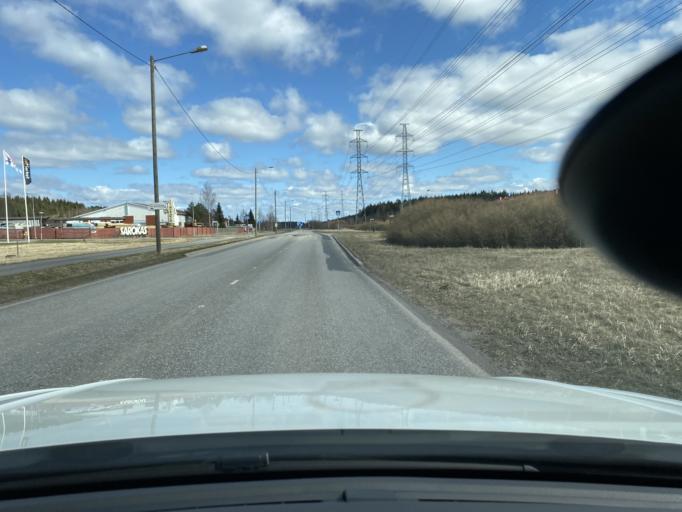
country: FI
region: Varsinais-Suomi
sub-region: Turku
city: Turku
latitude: 60.4729
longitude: 22.3136
